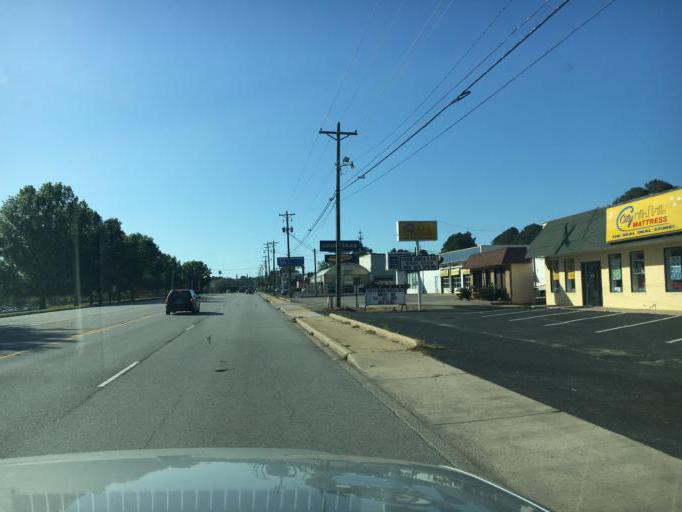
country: US
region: South Carolina
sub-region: Lexington County
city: Seven Oaks
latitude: 34.0509
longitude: -81.1565
